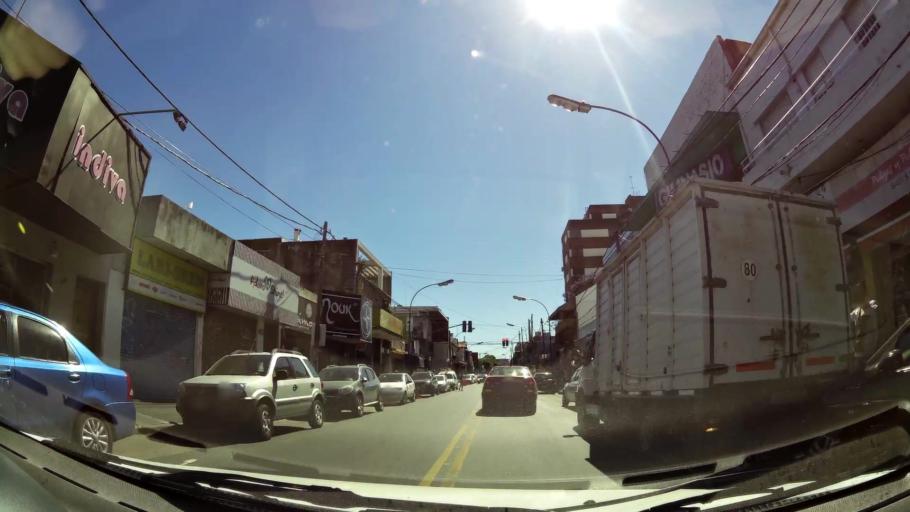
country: AR
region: Buenos Aires
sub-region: Partido de Vicente Lopez
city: Olivos
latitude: -34.5281
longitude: -58.5196
